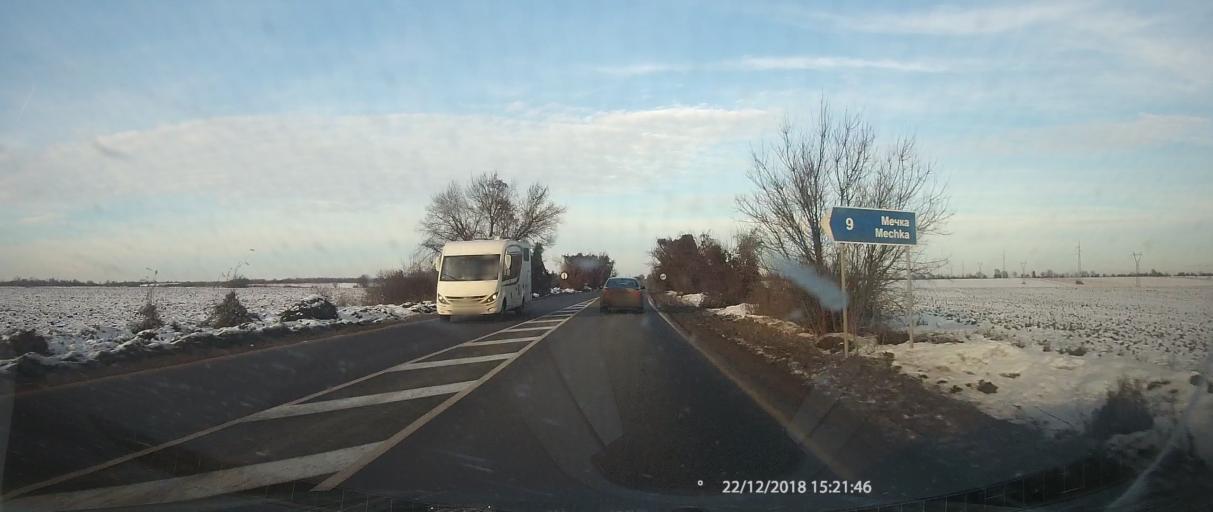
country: BG
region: Ruse
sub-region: Obshtina Ivanovo
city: Ivanovo
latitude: 43.6878
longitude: 25.9096
